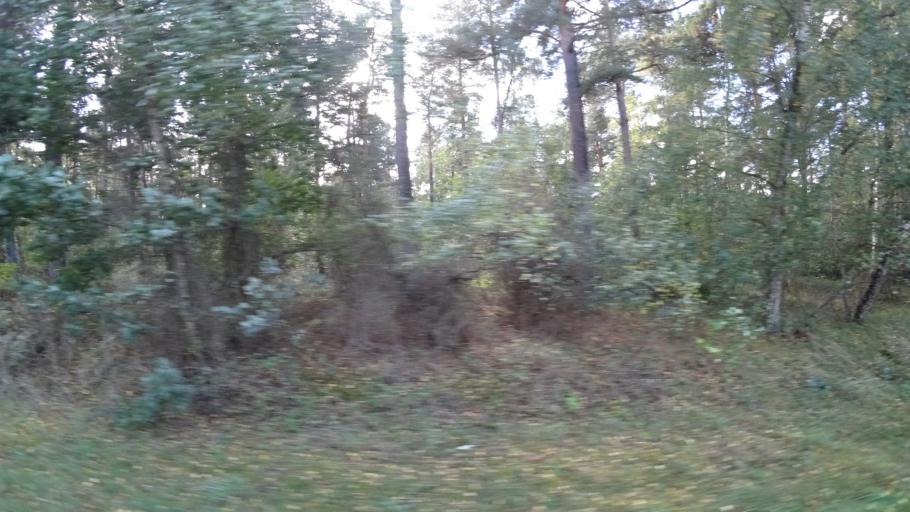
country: SE
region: Skane
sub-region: Kavlinge Kommun
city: Loddekopinge
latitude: 55.7595
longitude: 12.9893
